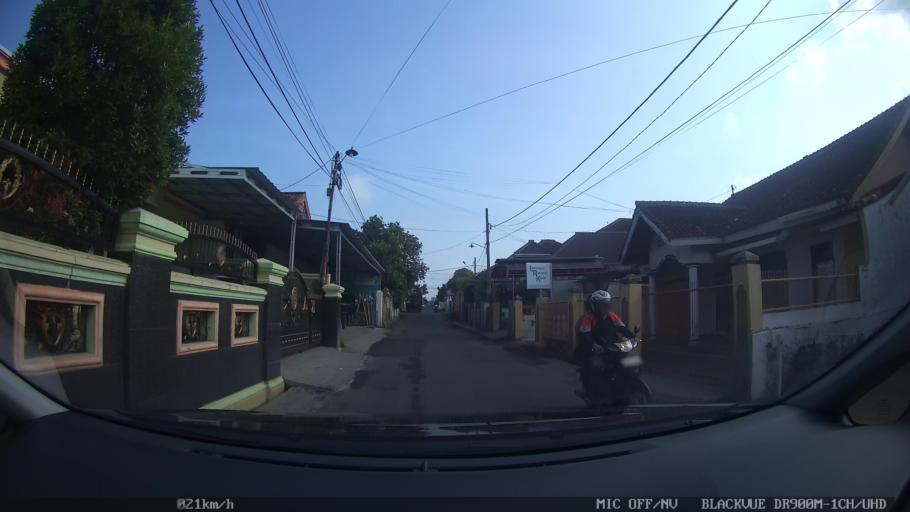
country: ID
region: Lampung
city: Kedaton
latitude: -5.3968
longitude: 105.2635
